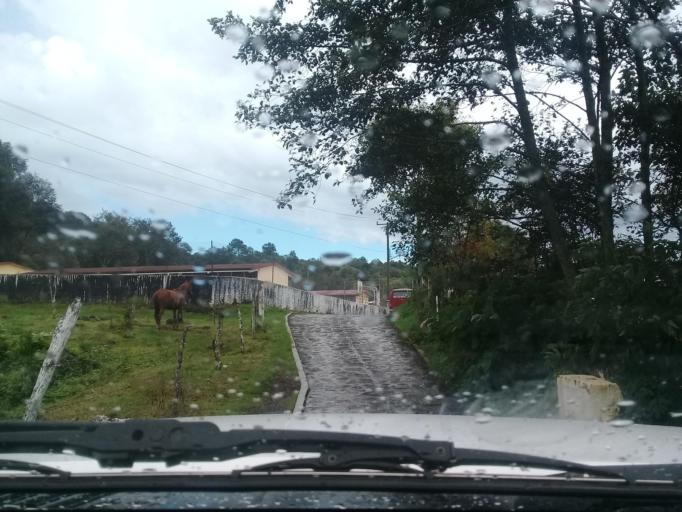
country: MX
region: Veracruz
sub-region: Acajete
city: La Joya
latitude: 19.6184
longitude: -97.0015
